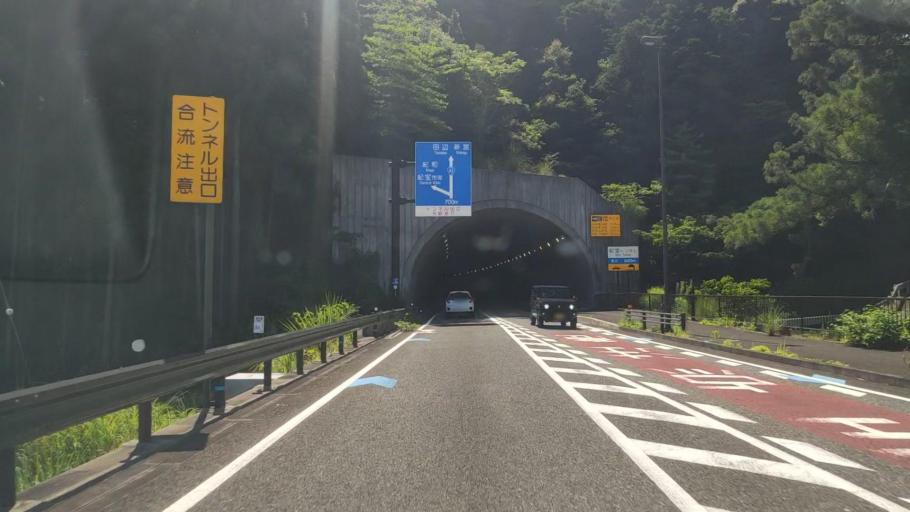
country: JP
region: Wakayama
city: Shingu
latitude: 33.7404
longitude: 135.9941
